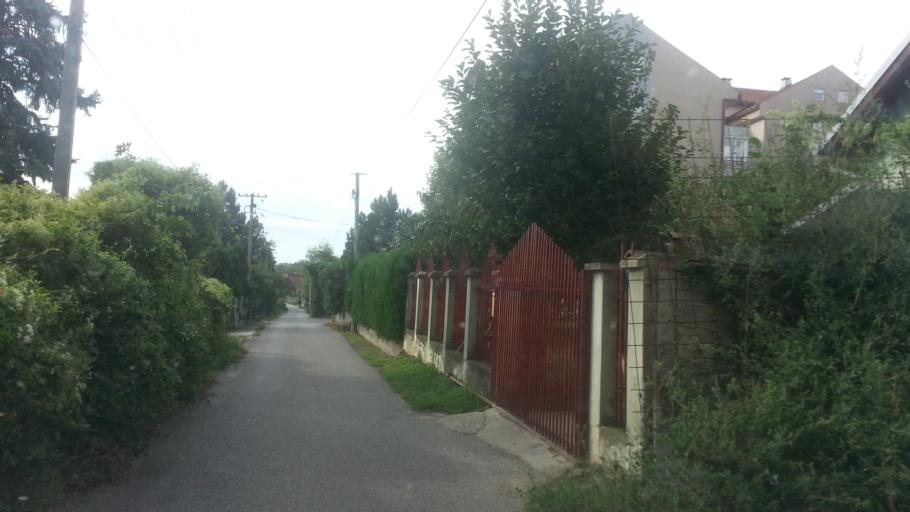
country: RS
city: Novi Banovci
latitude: 44.9660
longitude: 20.2824
